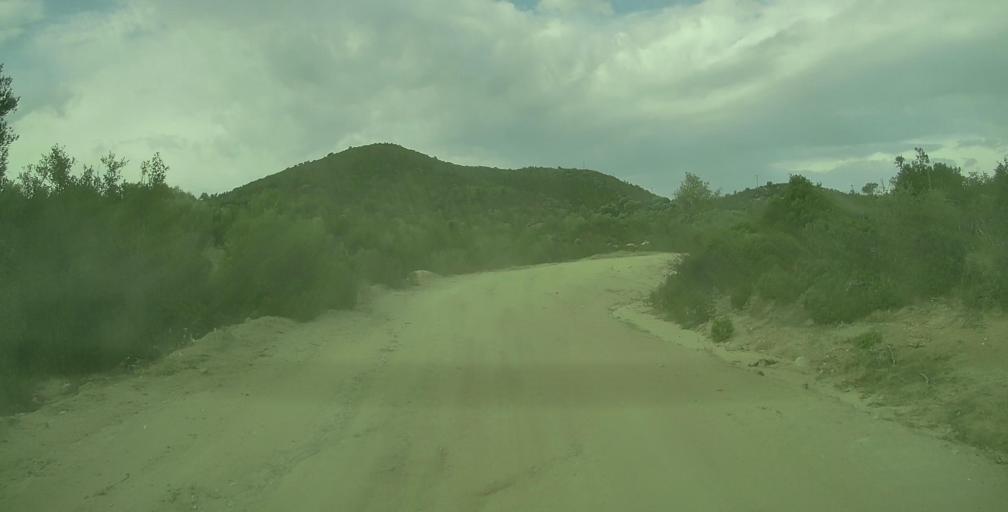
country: GR
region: Central Macedonia
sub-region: Nomos Chalkidikis
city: Sykia
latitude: 40.0132
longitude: 23.9309
